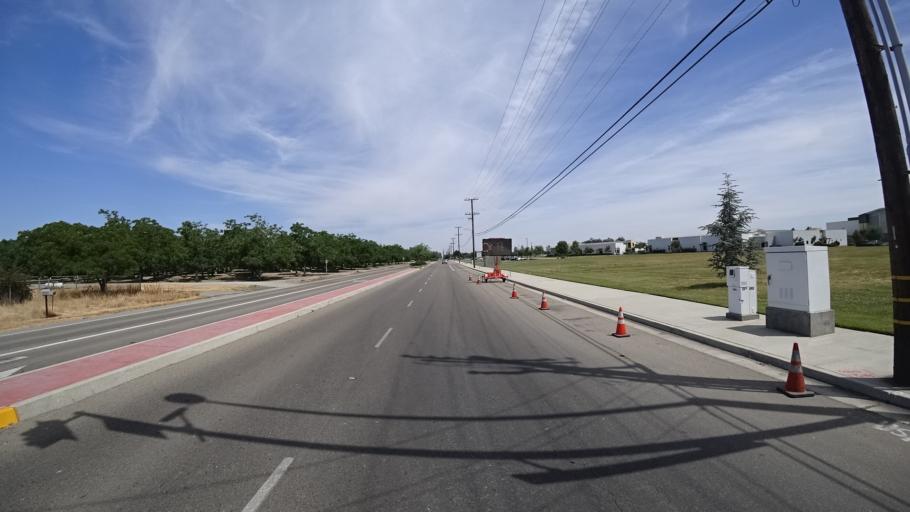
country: US
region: California
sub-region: Kings County
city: Armona
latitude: 36.3349
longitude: -119.6910
